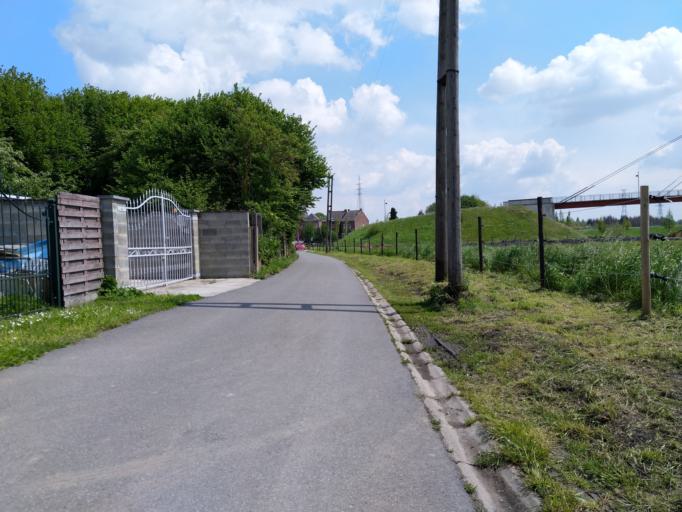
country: BE
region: Wallonia
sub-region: Province du Hainaut
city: Roeulx
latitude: 50.4750
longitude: 4.0655
